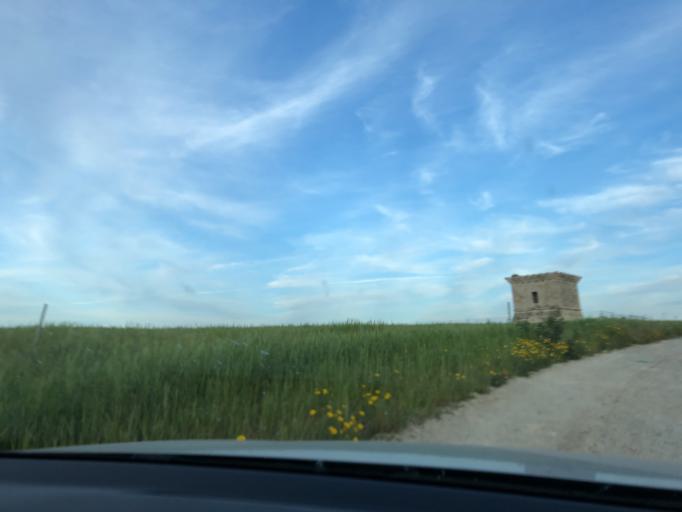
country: CY
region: Larnaka
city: Perivolia
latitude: 34.8328
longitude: 33.6011
